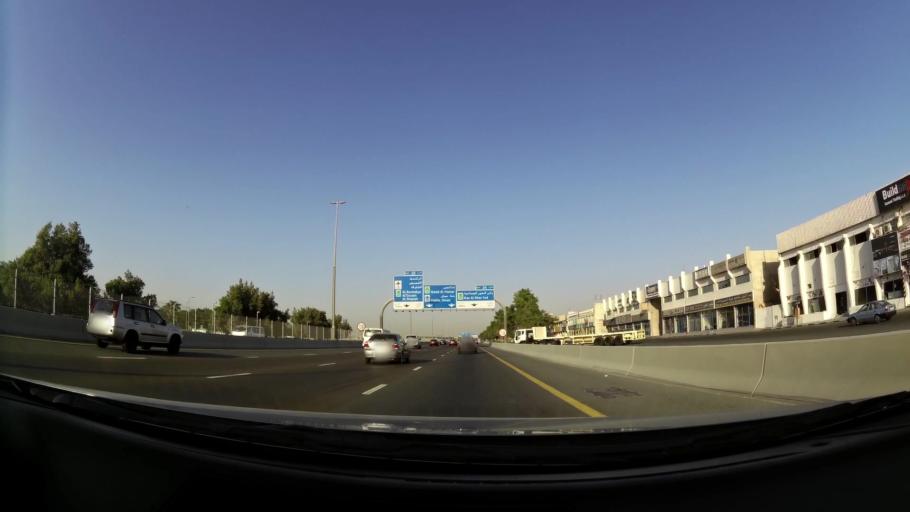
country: AE
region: Ash Shariqah
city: Sharjah
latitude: 25.1856
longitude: 55.3584
